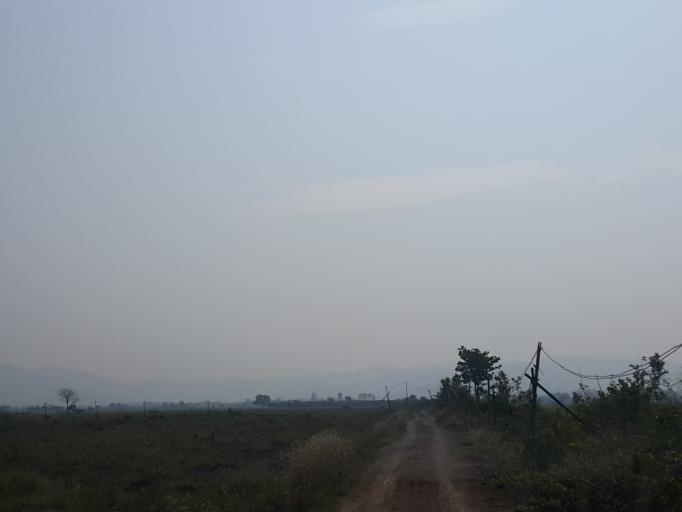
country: TH
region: Chiang Mai
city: San Kamphaeng
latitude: 18.7800
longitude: 99.1352
